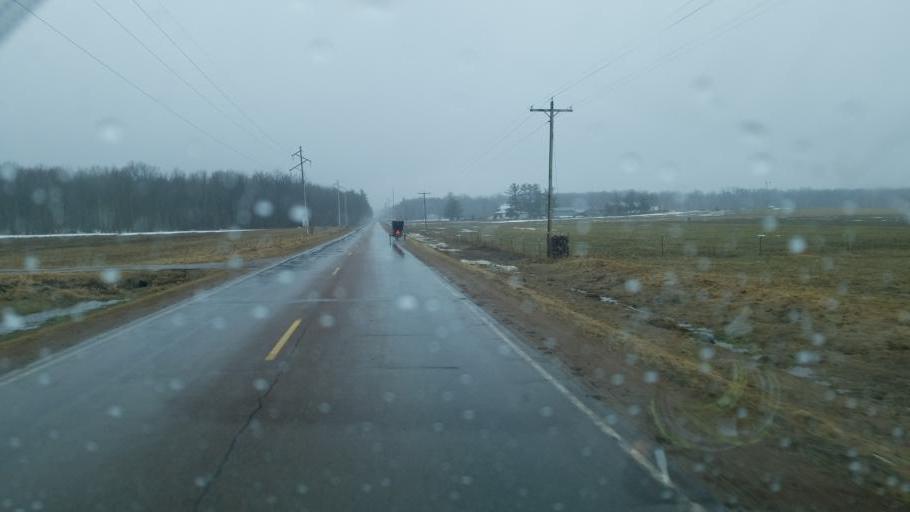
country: US
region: Wisconsin
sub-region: Clark County
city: Neillsville
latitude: 44.5307
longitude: -90.3964
